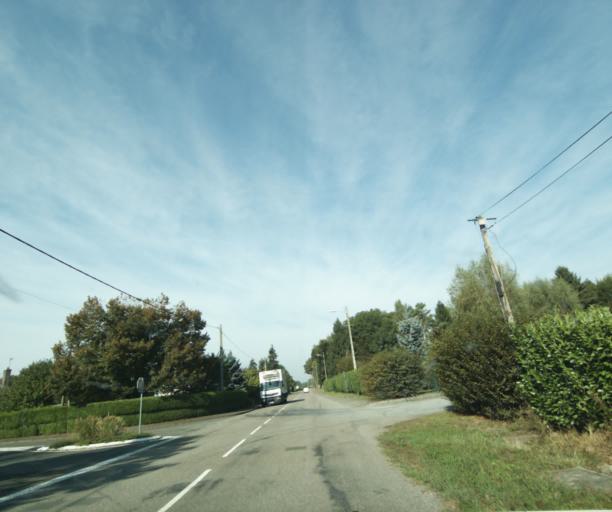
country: FR
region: Bourgogne
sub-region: Departement de Saone-et-Loire
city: Genelard
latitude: 46.5759
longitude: 4.2525
